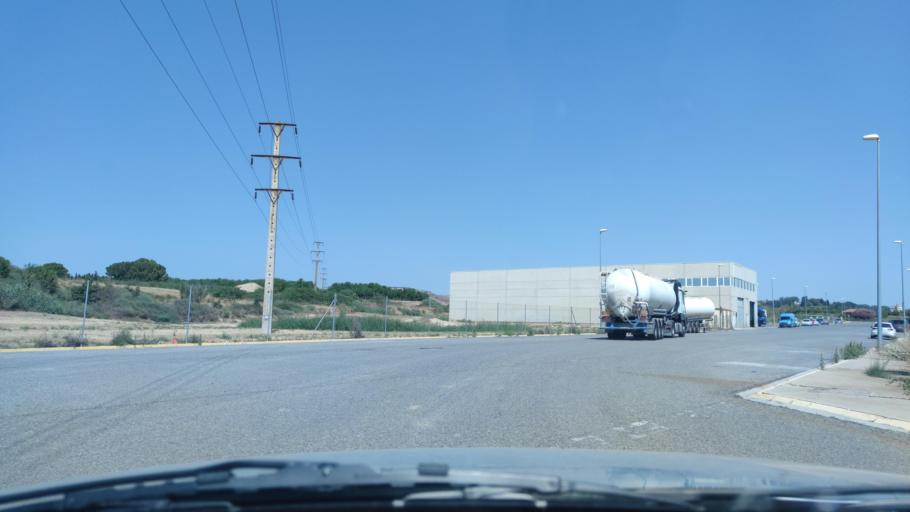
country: ES
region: Catalonia
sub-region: Provincia de Lleida
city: Torrefarrera
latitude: 41.6662
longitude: 0.5977
